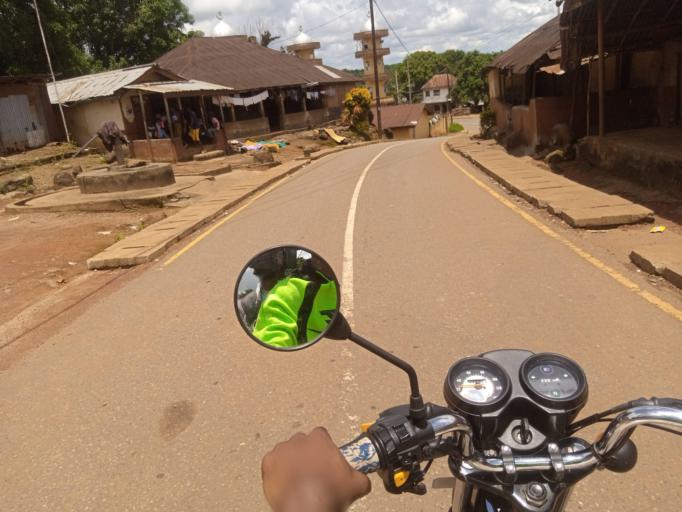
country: SL
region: Northern Province
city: Port Loko
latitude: 8.7638
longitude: -12.7906
